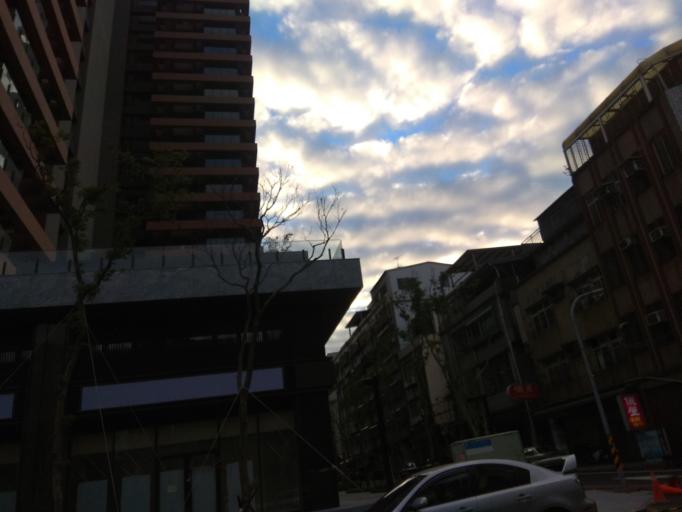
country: TW
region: Taiwan
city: Taoyuan City
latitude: 24.9945
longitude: 121.3078
